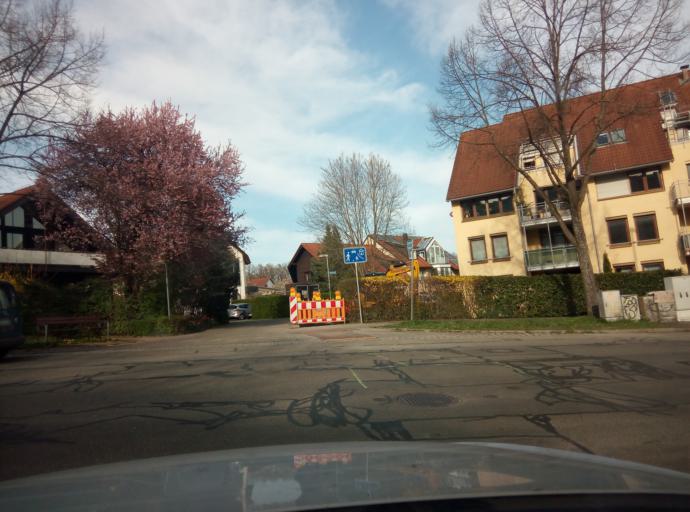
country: DE
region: Baden-Wuerttemberg
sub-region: Tuebingen Region
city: Tuebingen
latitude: 48.5449
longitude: 9.0638
